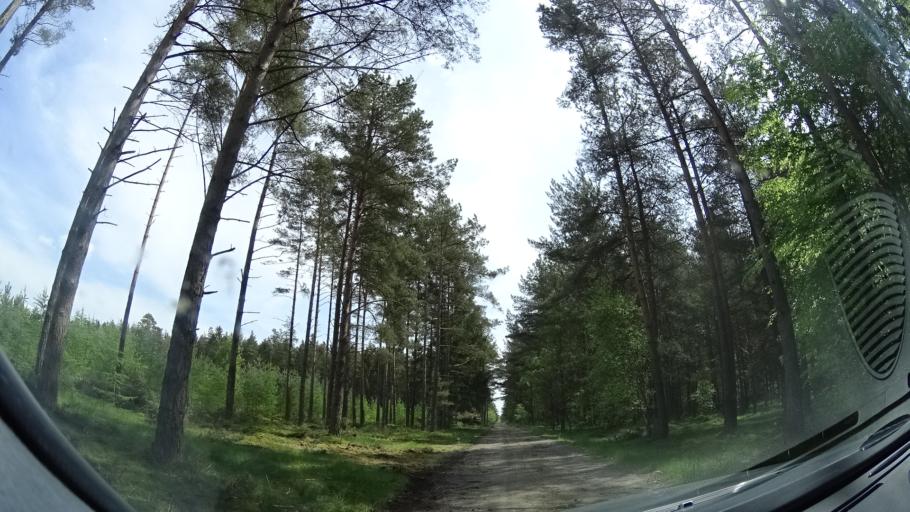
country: SE
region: Skane
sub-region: Sjobo Kommun
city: Sjoebo
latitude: 55.6692
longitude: 13.6429
